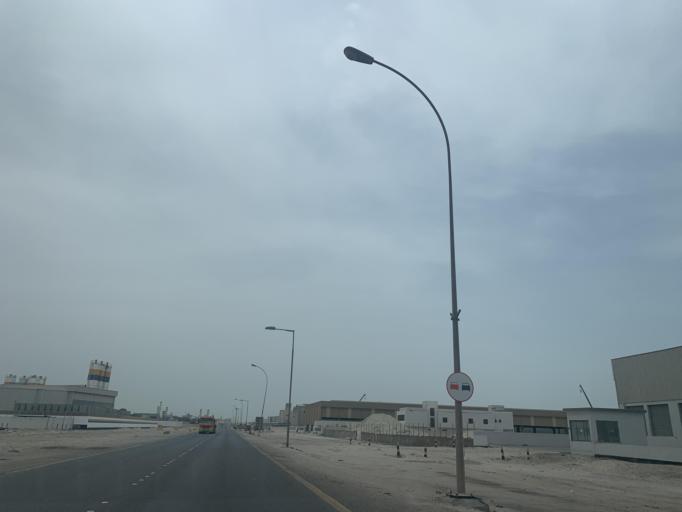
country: BH
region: Muharraq
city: Al Hadd
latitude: 26.2053
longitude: 50.6765
